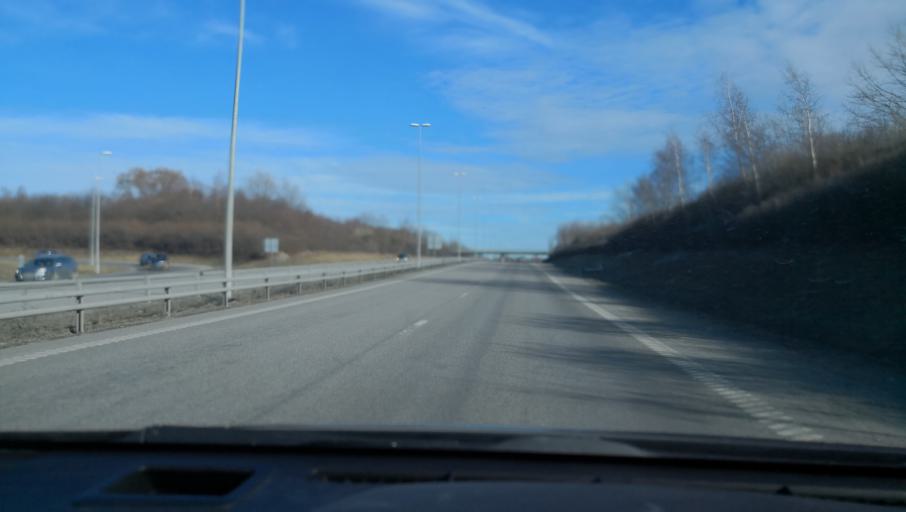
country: SE
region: Uppsala
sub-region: Uppsala Kommun
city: Gamla Uppsala
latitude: 59.8807
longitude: 17.6370
